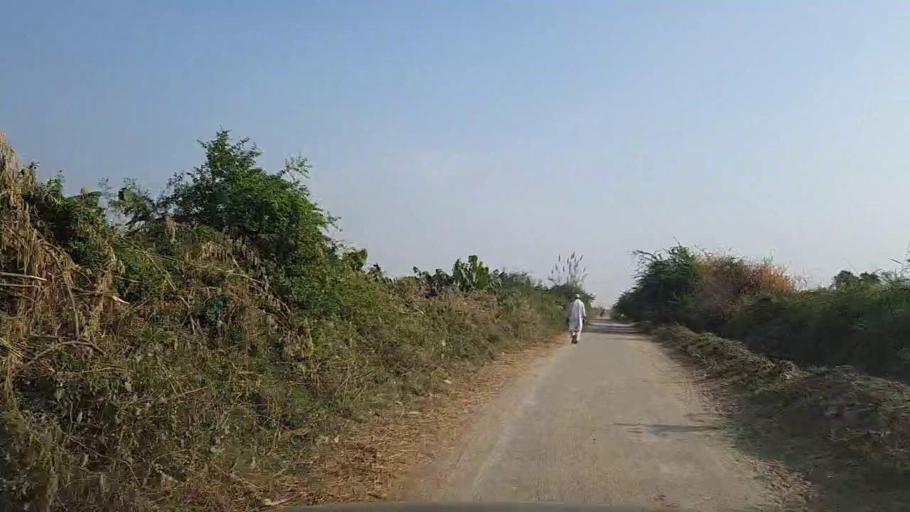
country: PK
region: Sindh
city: Thatta
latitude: 24.6511
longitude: 67.9235
